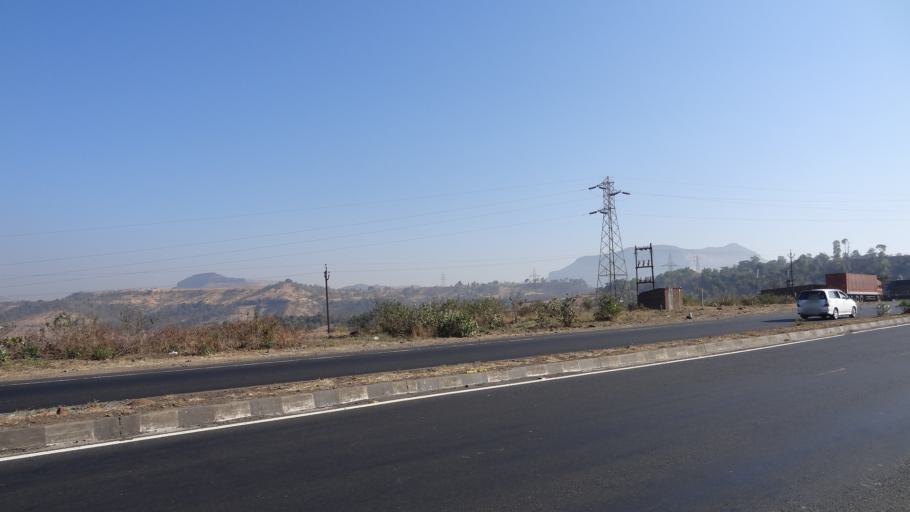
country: IN
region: Maharashtra
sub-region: Nashik Division
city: Igatpuri
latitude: 19.6977
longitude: 73.5174
